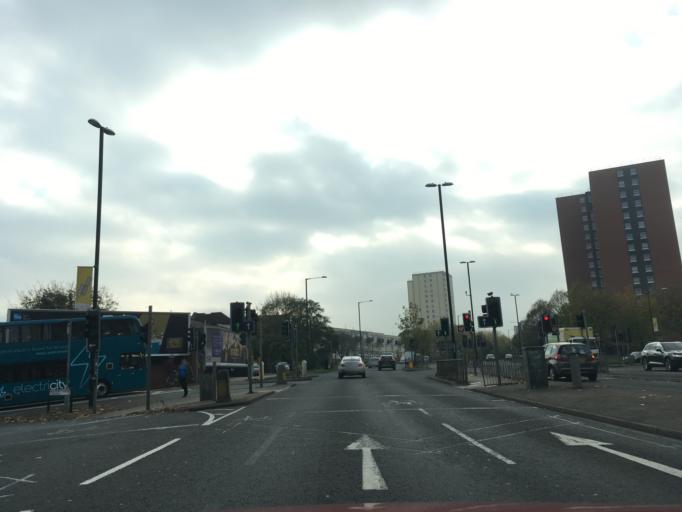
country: GB
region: England
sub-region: Bristol
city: Bristol
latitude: 51.4638
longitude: -2.5713
